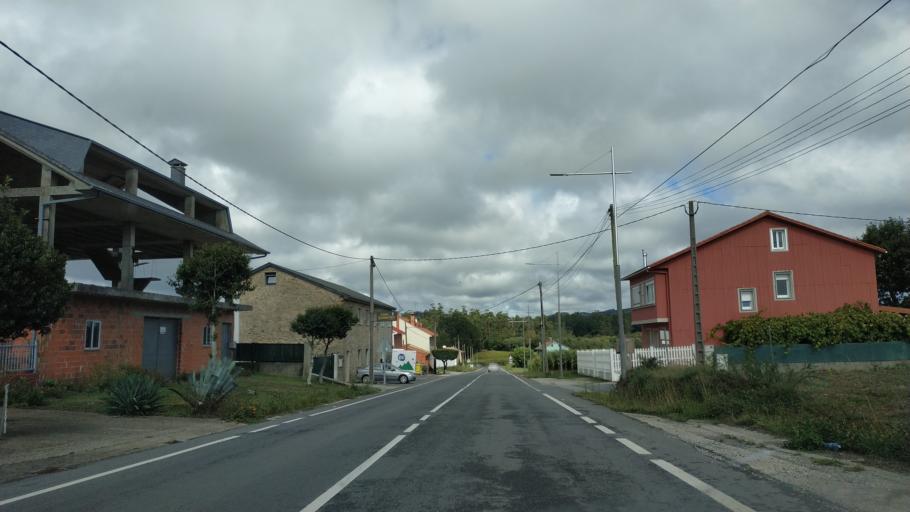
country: ES
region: Galicia
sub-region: Provincia da Coruna
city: Cerceda
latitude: 43.1442
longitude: -8.5714
